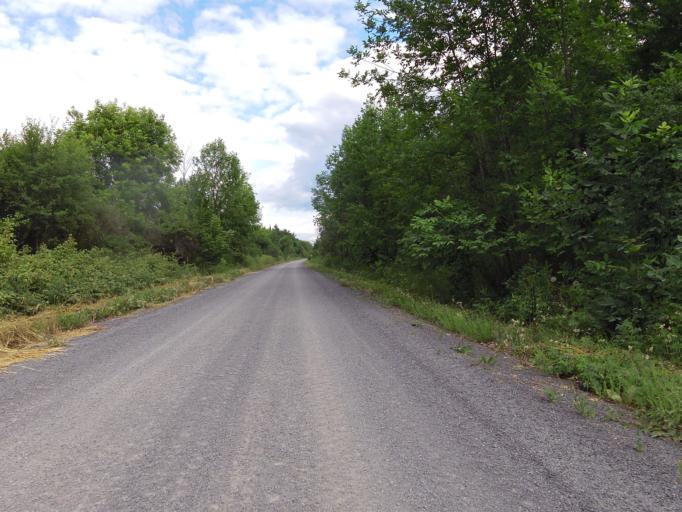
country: CA
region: Ontario
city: Arnprior
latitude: 45.2849
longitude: -76.2486
